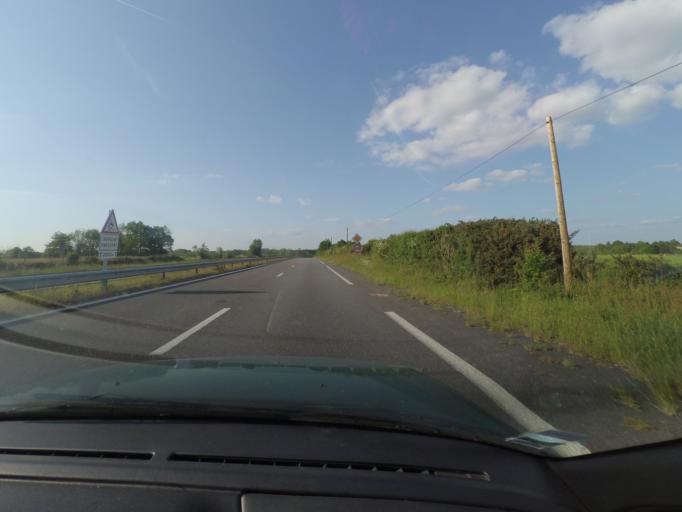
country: FR
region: Pays de la Loire
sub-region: Departement de la Vendee
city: Saligny
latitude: 46.8149
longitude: -1.4304
